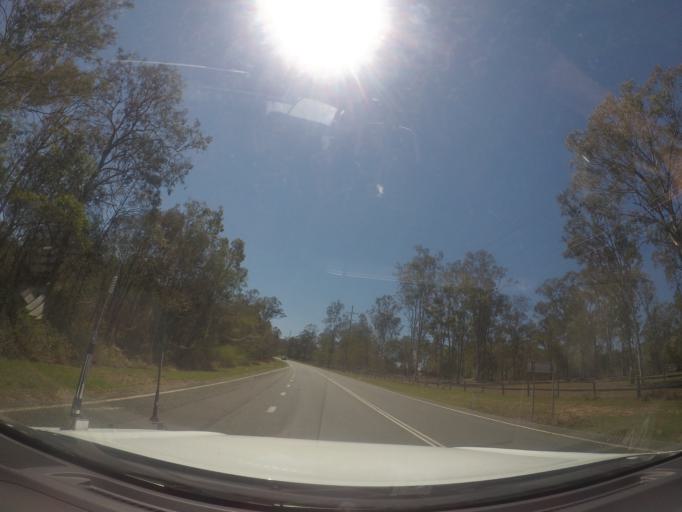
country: AU
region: Queensland
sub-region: Logan
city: North Maclean
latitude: -27.8101
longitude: 153.0413
